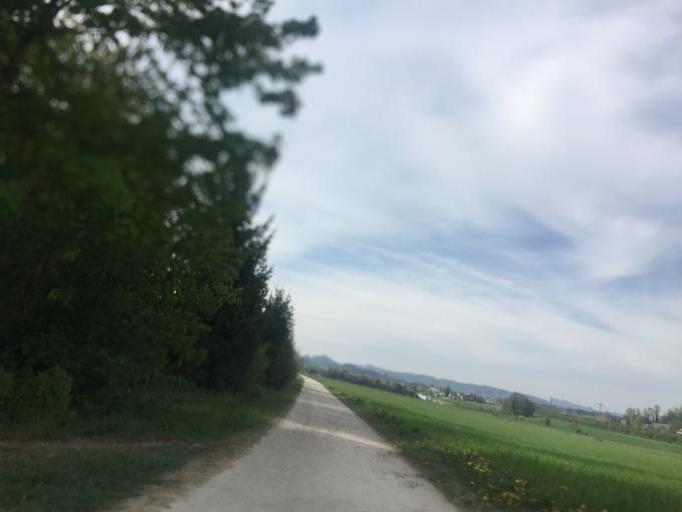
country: CH
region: Bern
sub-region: Bern-Mittelland District
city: Munsingen
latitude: 46.8828
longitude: 7.5533
